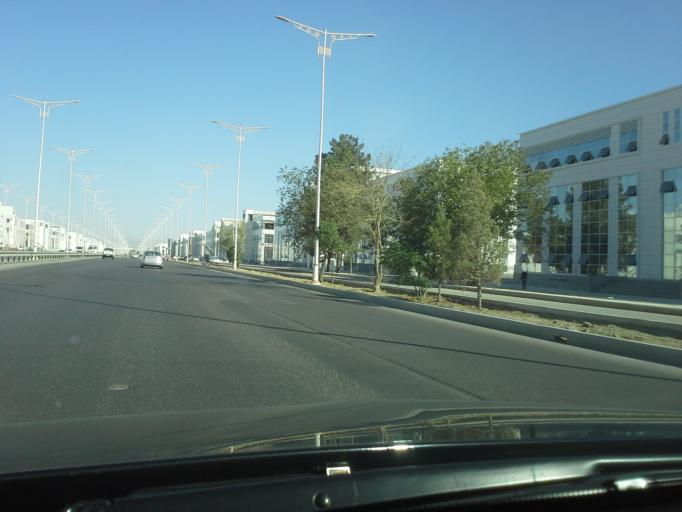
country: TM
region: Ahal
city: Ashgabat
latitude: 37.9716
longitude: 58.4024
